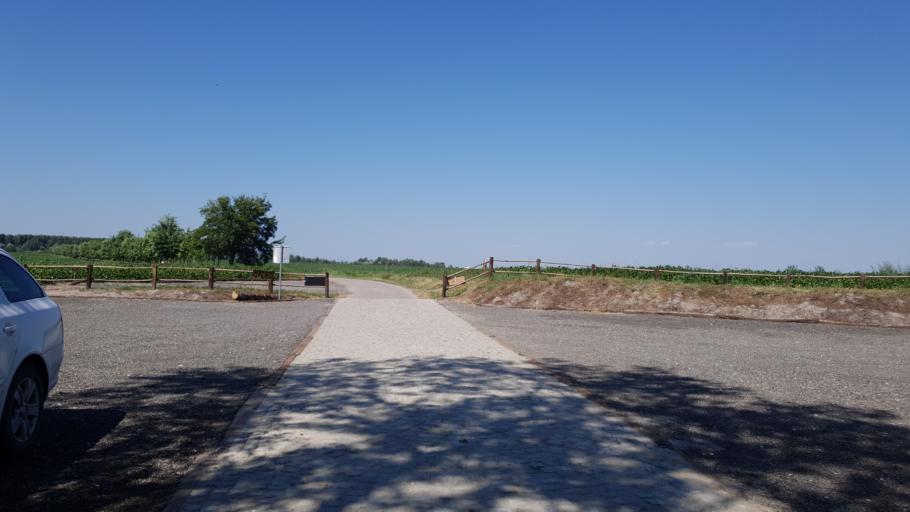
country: RS
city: Beska
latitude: 45.1923
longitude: 20.0681
